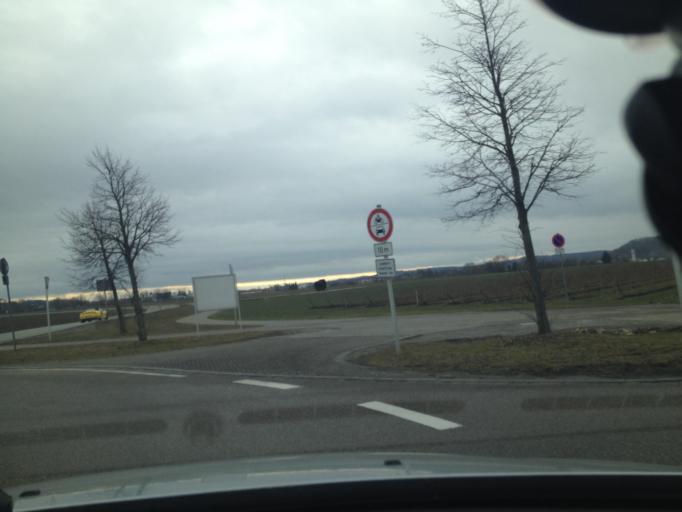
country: DE
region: Bavaria
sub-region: Swabia
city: Gersthofen
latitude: 48.4141
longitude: 10.8398
